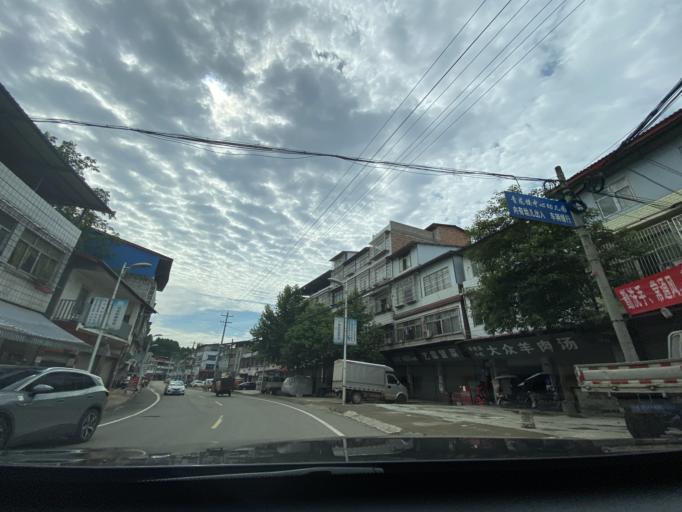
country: CN
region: Sichuan
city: Jiancheng
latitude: 30.4874
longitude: 104.6311
